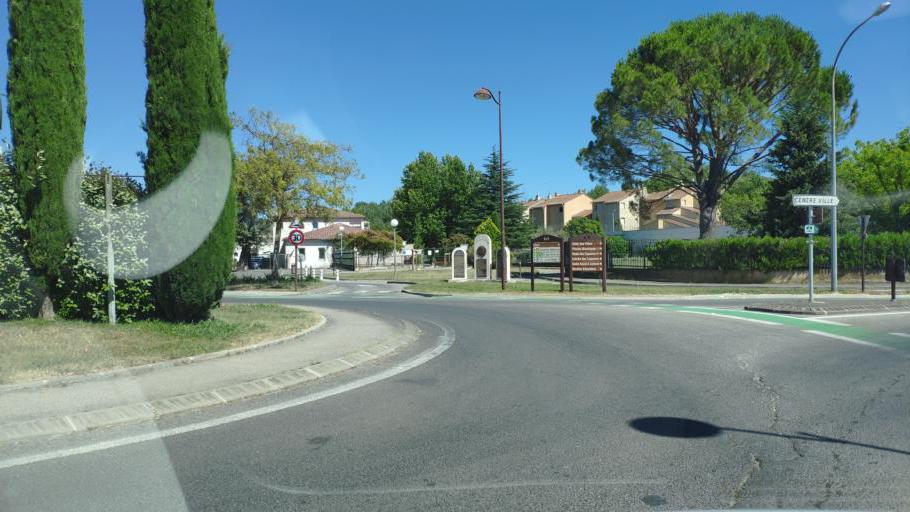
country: FR
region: Provence-Alpes-Cote d'Azur
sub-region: Departement du Vaucluse
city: L'Isle-sur-la-Sorgue
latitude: 43.9283
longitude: 5.0525
